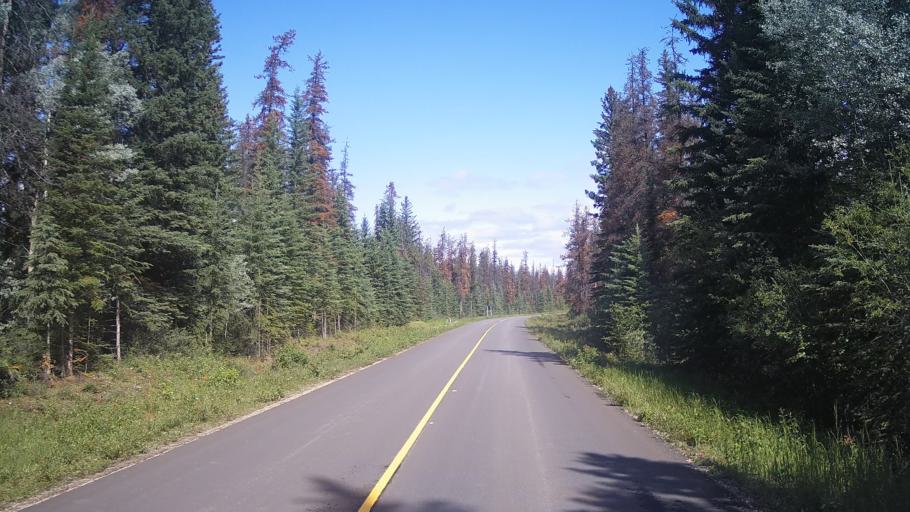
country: CA
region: Alberta
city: Jasper Park Lodge
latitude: 52.7462
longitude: -117.9721
